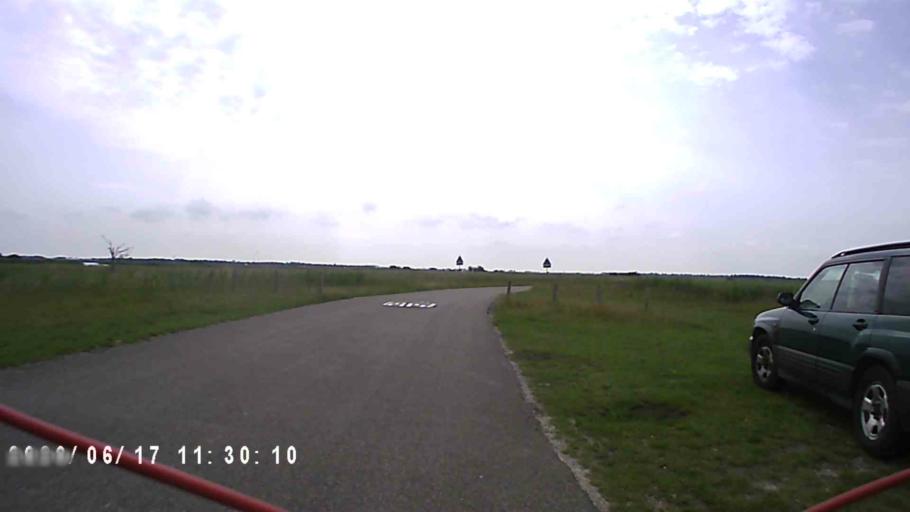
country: NL
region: Groningen
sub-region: Gemeente De Marne
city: Ulrum
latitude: 53.3678
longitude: 6.2430
